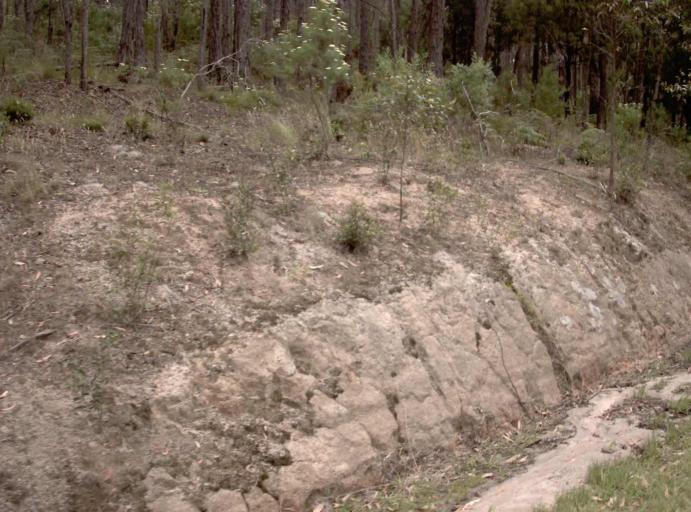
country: AU
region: Victoria
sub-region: Latrobe
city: Traralgon
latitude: -38.4938
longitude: 146.6433
